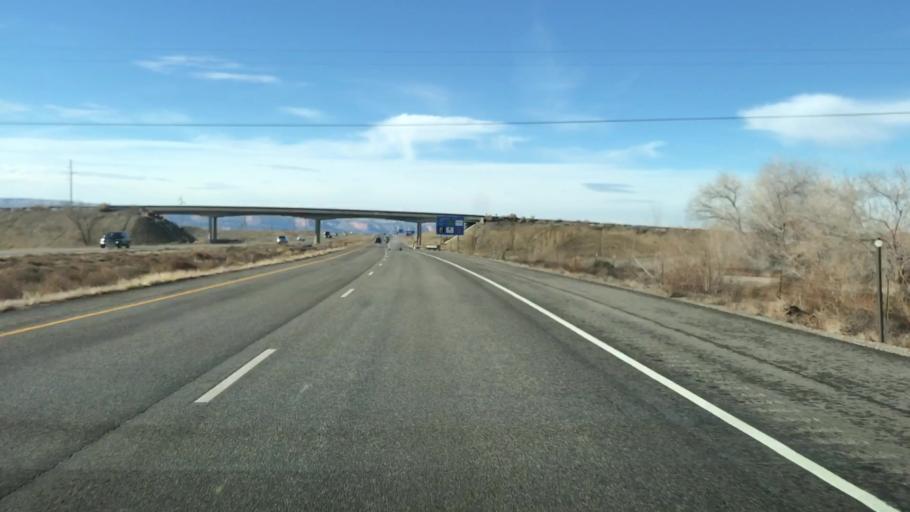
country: US
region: Colorado
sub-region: Mesa County
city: Fruitvale
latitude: 39.1086
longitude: -108.5095
